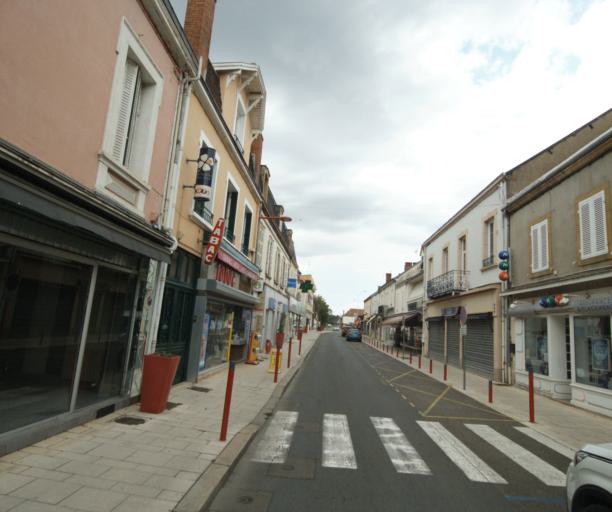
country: FR
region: Bourgogne
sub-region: Departement de Saone-et-Loire
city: Gueugnon
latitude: 46.6012
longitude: 4.0616
